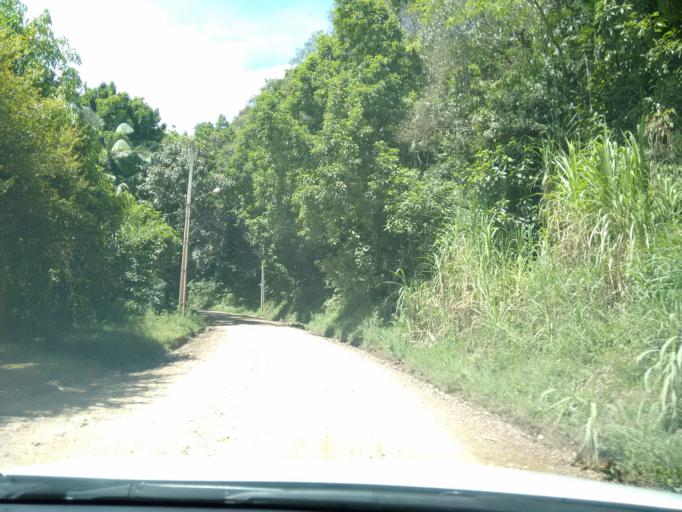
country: BR
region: Santa Catarina
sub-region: Pomerode
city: Pomerode
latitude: -26.7210
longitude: -49.1403
